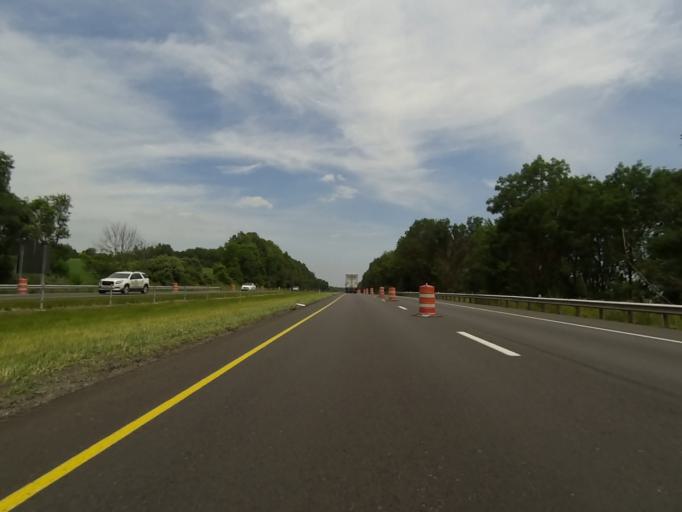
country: US
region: Ohio
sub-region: Portage County
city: Ravenna
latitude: 41.1058
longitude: -81.2046
